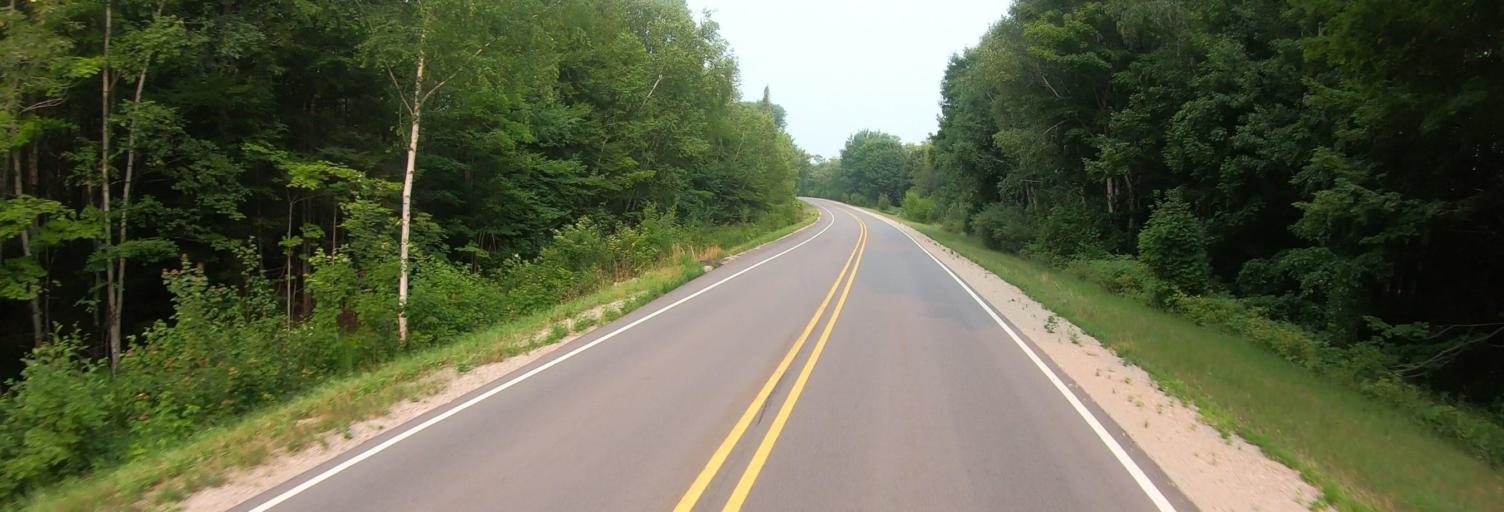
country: US
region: Michigan
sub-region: Luce County
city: Newberry
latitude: 46.4863
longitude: -85.0346
